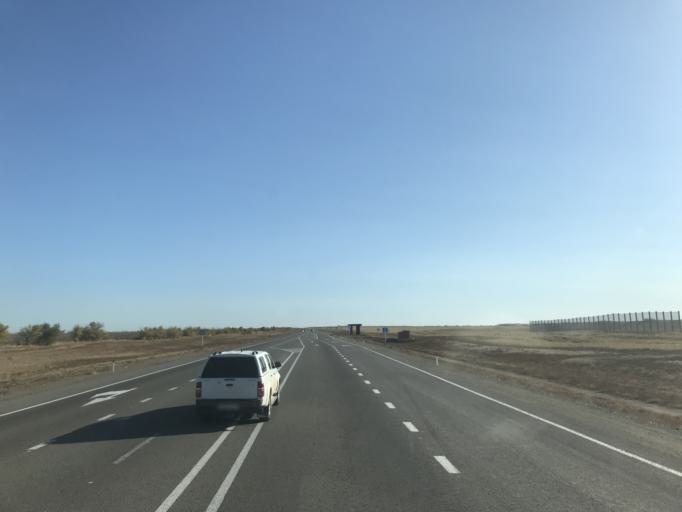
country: KZ
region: Pavlodar
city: Koktobe
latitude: 51.8135
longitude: 77.4717
